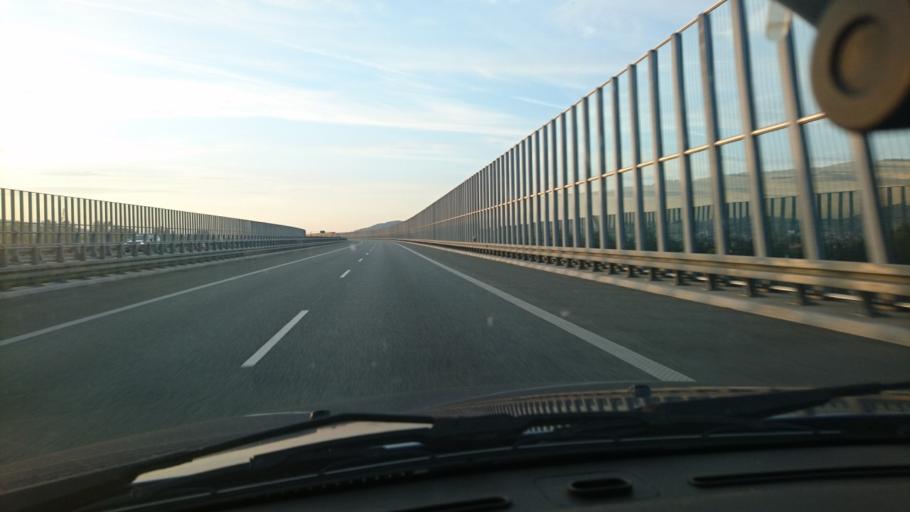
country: PL
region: Silesian Voivodeship
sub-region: Powiat bielski
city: Rybarzowice
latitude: 49.7313
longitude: 19.1164
